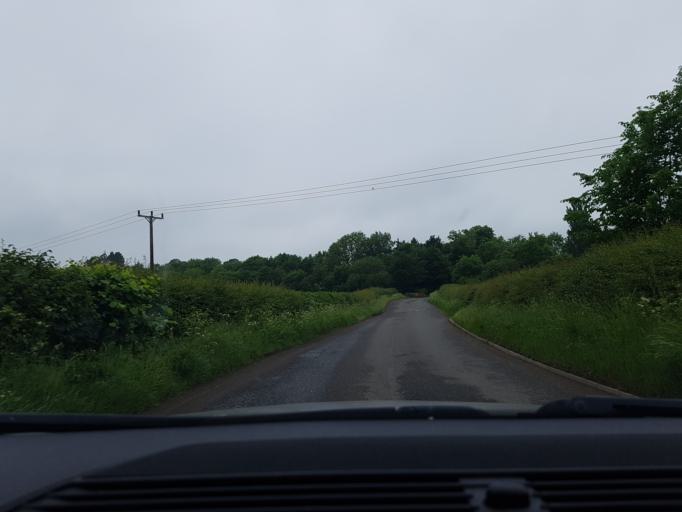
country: GB
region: England
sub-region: Buckinghamshire
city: Steeple Claydon
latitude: 51.9304
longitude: -0.9676
